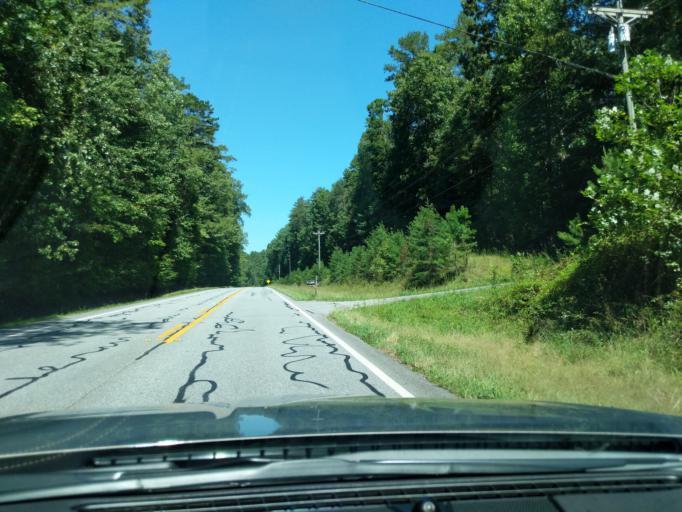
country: US
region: Georgia
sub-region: White County
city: Cleveland
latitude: 34.6729
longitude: -83.6542
